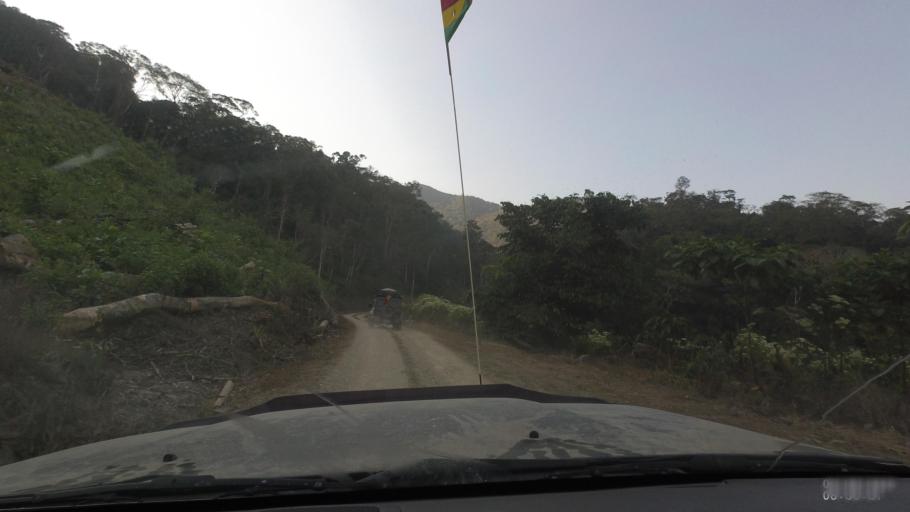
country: BO
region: La Paz
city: Quime
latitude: -16.5017
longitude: -66.7633
